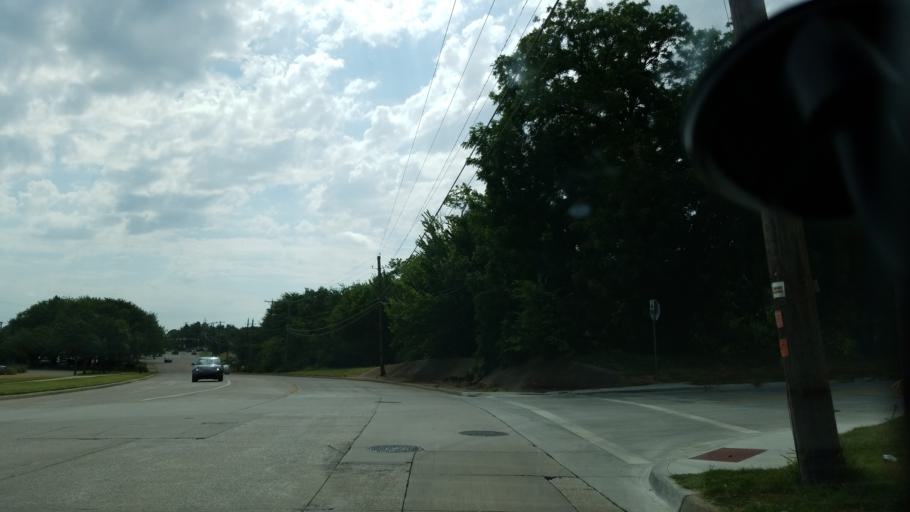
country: US
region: Texas
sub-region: Dallas County
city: Grand Prairie
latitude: 32.7489
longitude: -96.9983
